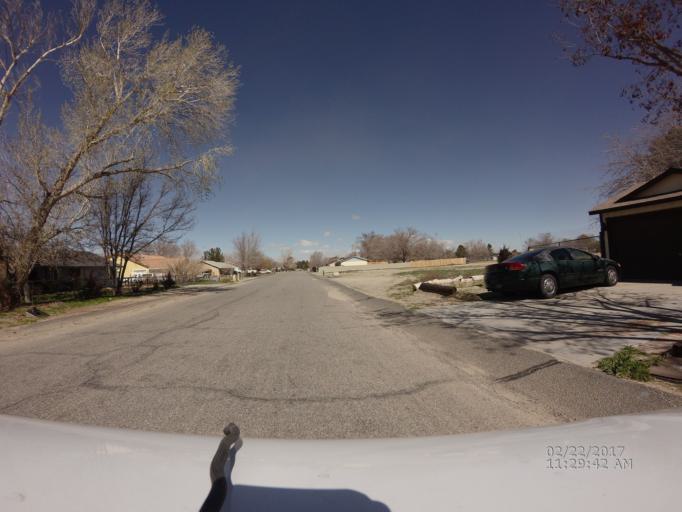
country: US
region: California
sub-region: Los Angeles County
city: Lake Los Angeles
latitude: 34.6215
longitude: -117.8170
